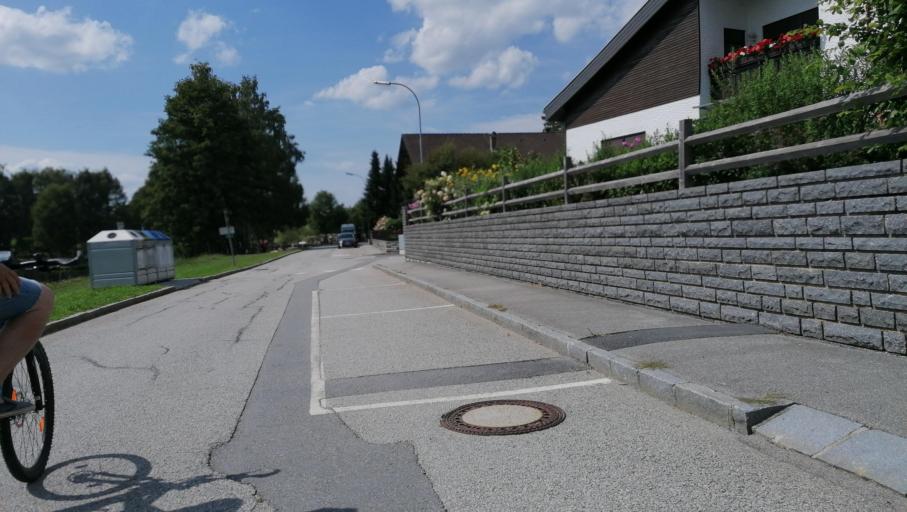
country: AT
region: Lower Austria
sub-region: Politischer Bezirk Gmund
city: Schrems
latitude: 48.7943
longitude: 15.0821
